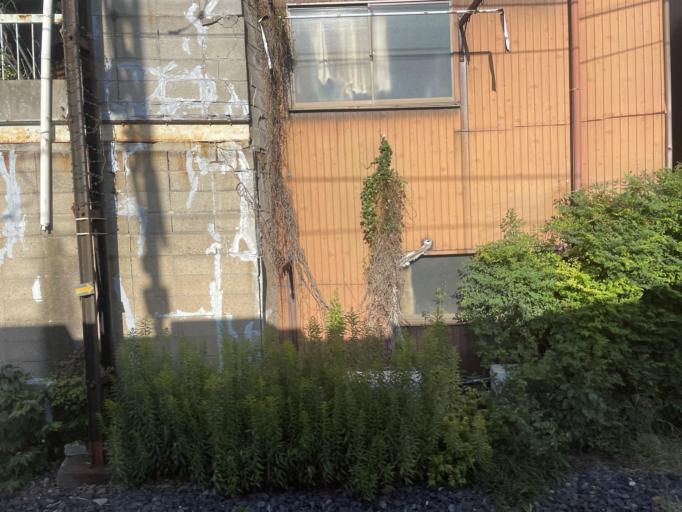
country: JP
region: Osaka
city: Osaka-shi
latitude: 34.6403
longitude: 135.4881
